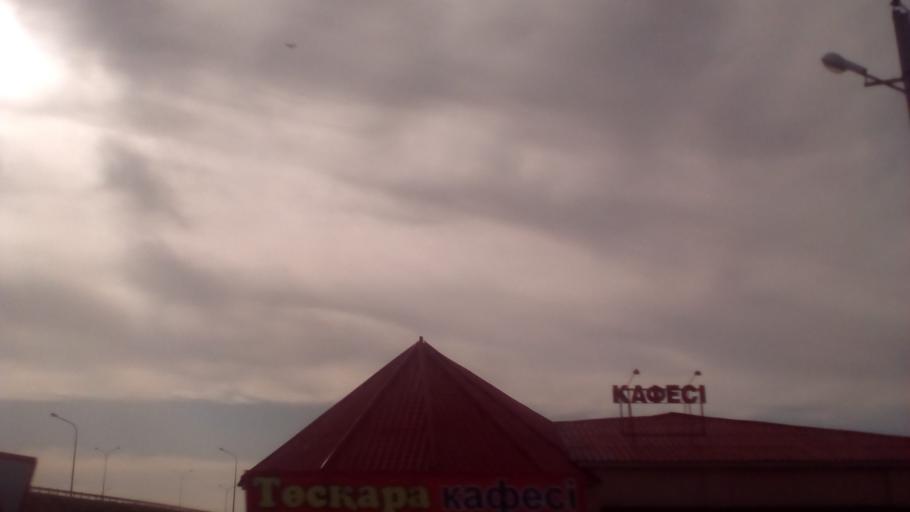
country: KZ
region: Ongtustik Qazaqstan
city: Temirlanovka
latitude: 42.7985
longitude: 69.1997
